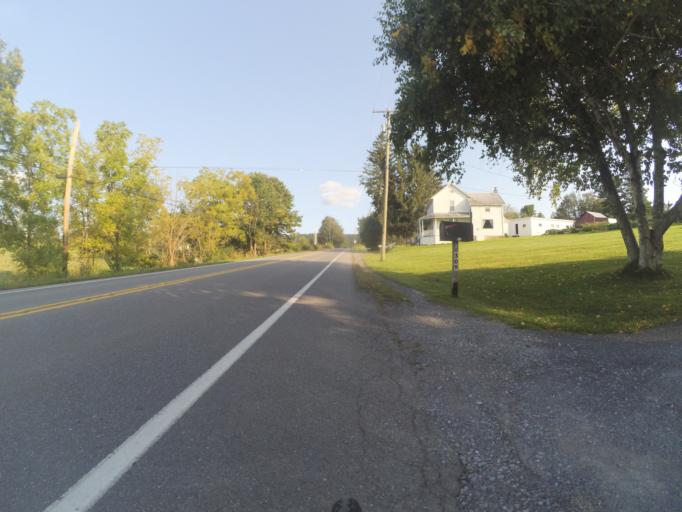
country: US
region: Pennsylvania
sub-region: Centre County
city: Centre Hall
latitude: 40.8069
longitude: -77.6322
